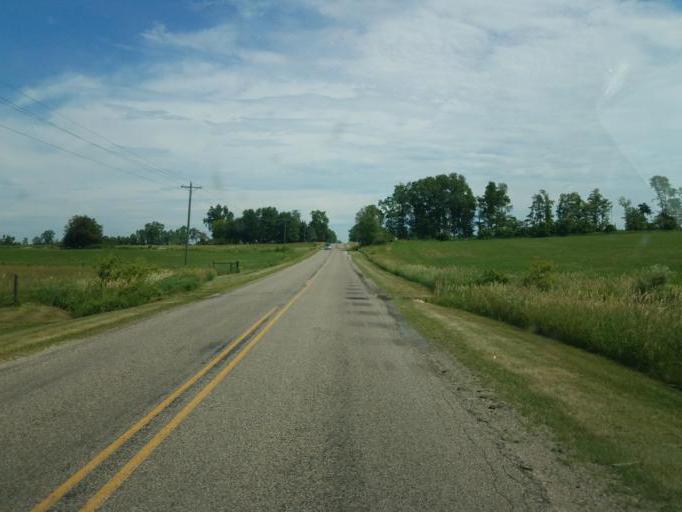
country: US
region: Michigan
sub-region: Barry County
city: Nashville
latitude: 42.6748
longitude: -85.0343
